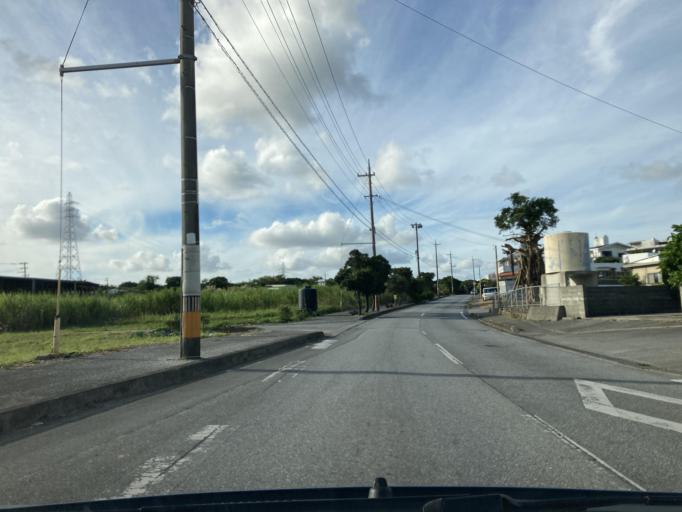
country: JP
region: Okinawa
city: Tomigusuku
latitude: 26.1435
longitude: 127.7466
